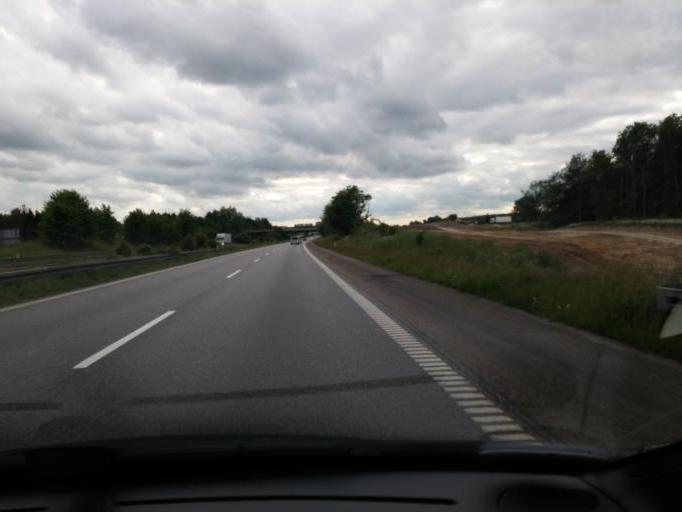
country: DK
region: Zealand
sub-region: Koge Kommune
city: Ejby
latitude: 55.4723
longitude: 12.0763
